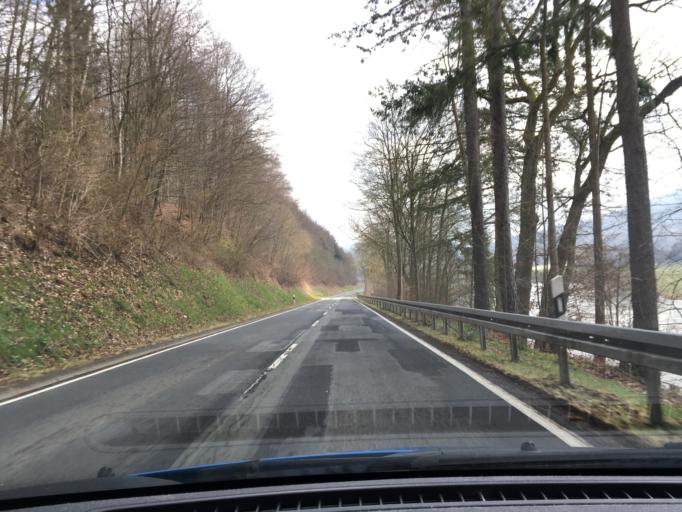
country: DE
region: Lower Saxony
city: Bodenfelde
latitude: 51.5664
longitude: 9.6024
